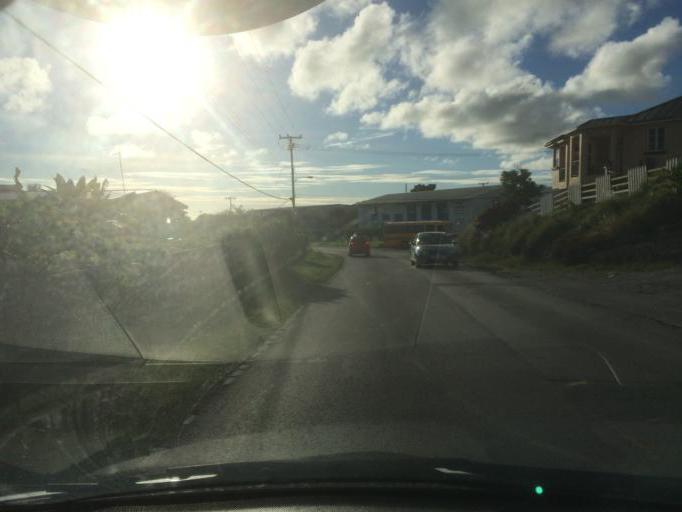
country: BB
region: Christ Church
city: Oistins
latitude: 13.0788
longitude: -59.5331
